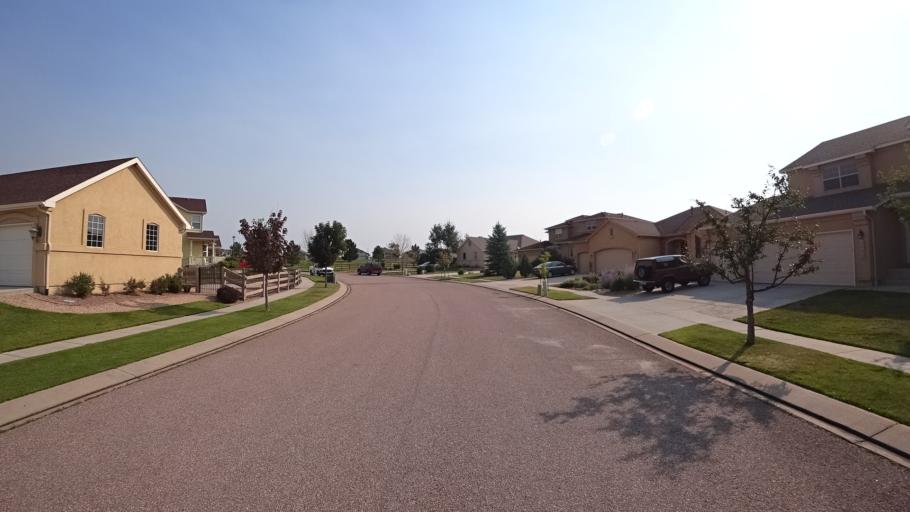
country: US
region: Colorado
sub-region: El Paso County
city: Black Forest
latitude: 38.9604
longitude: -104.7134
